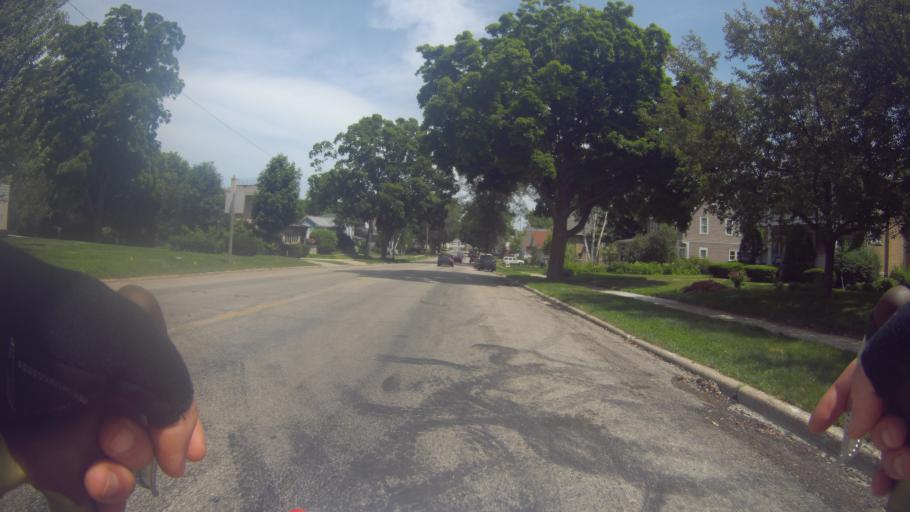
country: US
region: Wisconsin
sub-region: Jefferson County
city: Lake Mills
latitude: 43.0753
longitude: -88.9135
